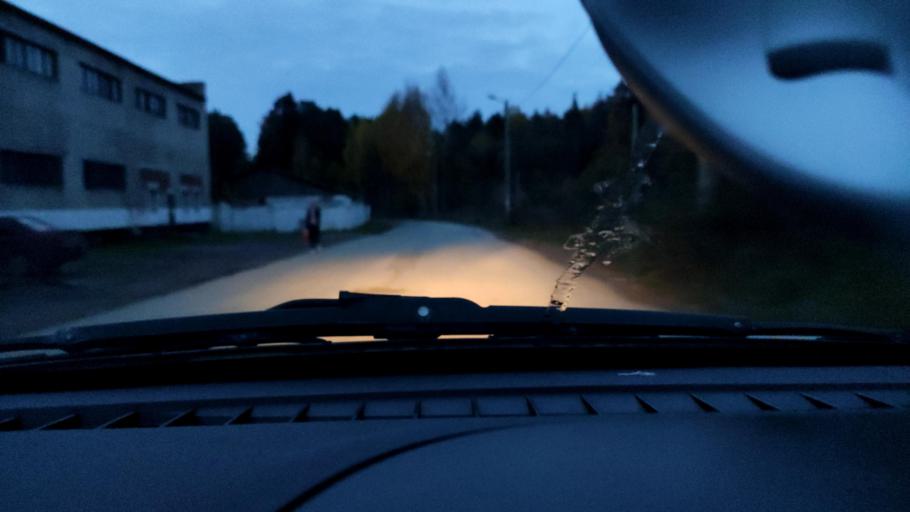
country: RU
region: Perm
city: Kondratovo
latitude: 58.0444
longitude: 56.1379
